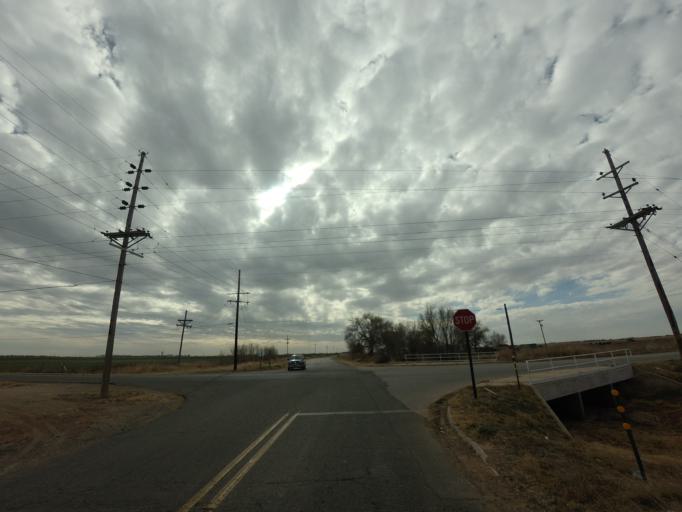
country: US
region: New Mexico
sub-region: Curry County
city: Clovis
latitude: 34.3905
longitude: -103.2318
